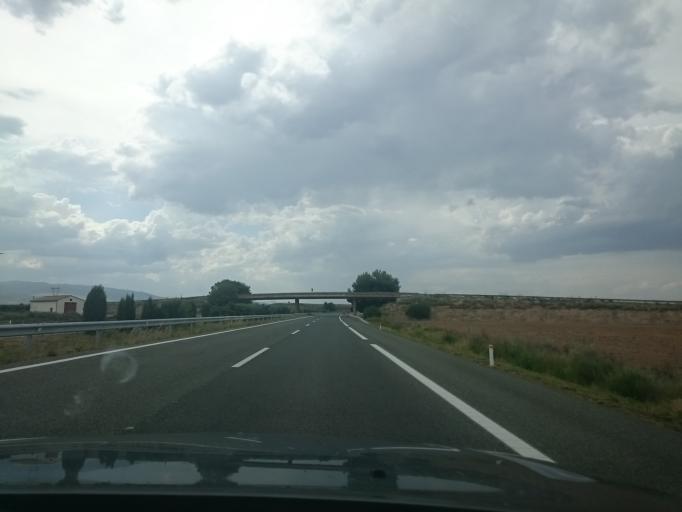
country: ES
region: Navarre
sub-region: Provincia de Navarra
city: Corella
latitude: 42.1534
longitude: -1.8061
